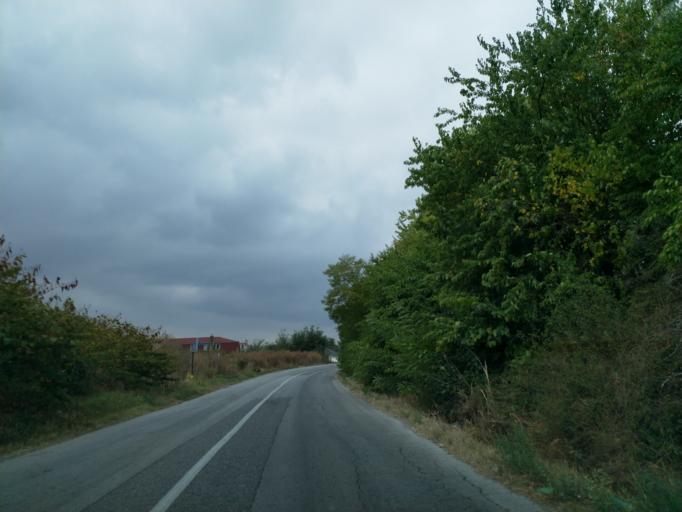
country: RS
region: Central Serbia
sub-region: Pomoravski Okrug
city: Jagodina
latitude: 43.9895
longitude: 21.2331
